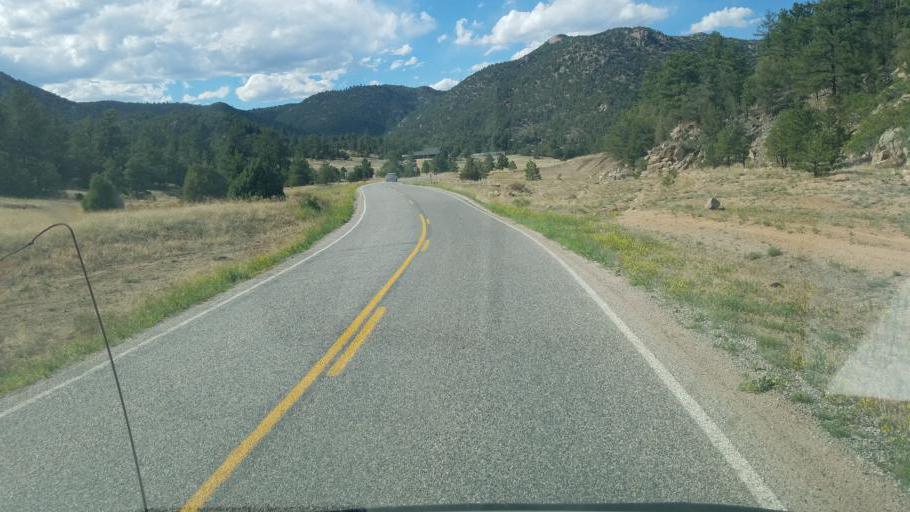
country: US
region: Colorado
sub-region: Fremont County
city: Canon City
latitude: 38.3816
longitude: -105.4558
